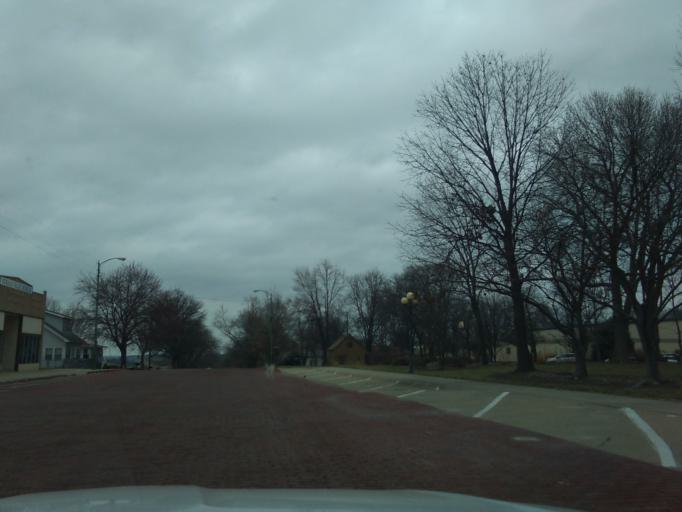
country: US
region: Nebraska
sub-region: Nemaha County
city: Auburn
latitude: 40.3855
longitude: -95.8454
